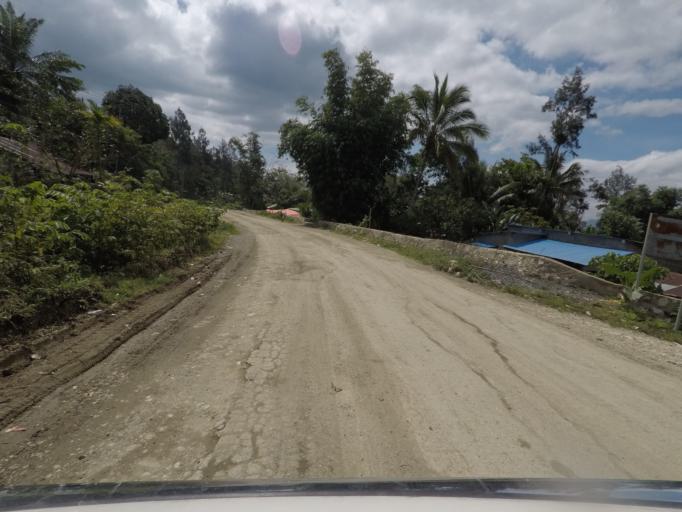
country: TL
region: Baucau
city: Venilale
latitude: -8.7402
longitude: 126.3755
